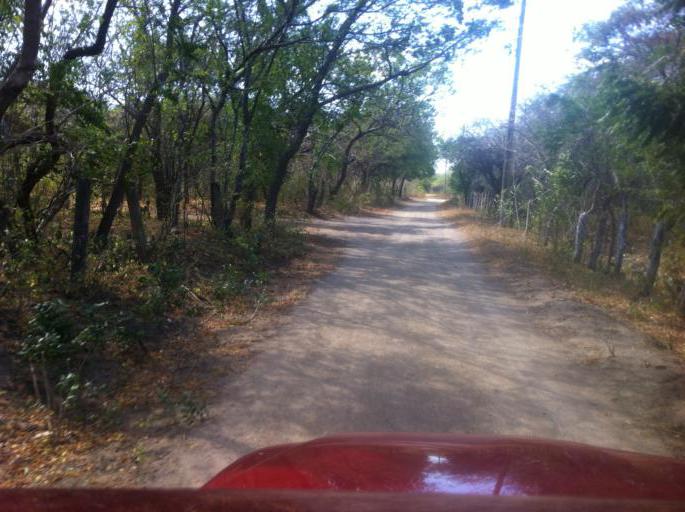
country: NI
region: Carazo
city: Santa Teresa
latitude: 11.6070
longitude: -86.3028
